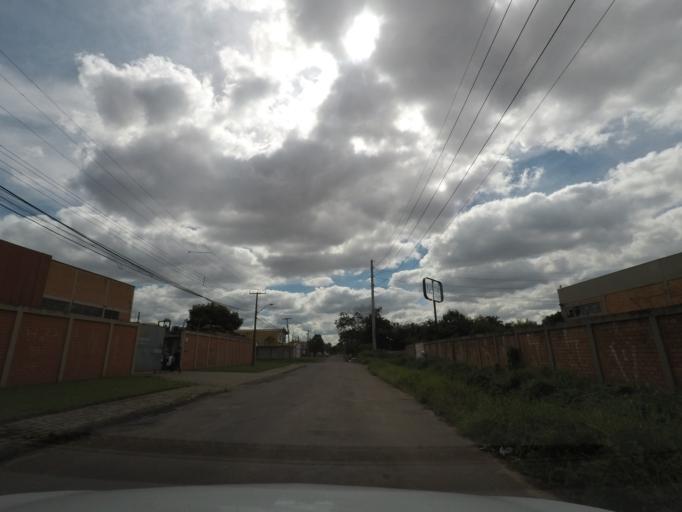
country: BR
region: Parana
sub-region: Sao Jose Dos Pinhais
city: Sao Jose dos Pinhais
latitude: -25.4906
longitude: -49.2317
